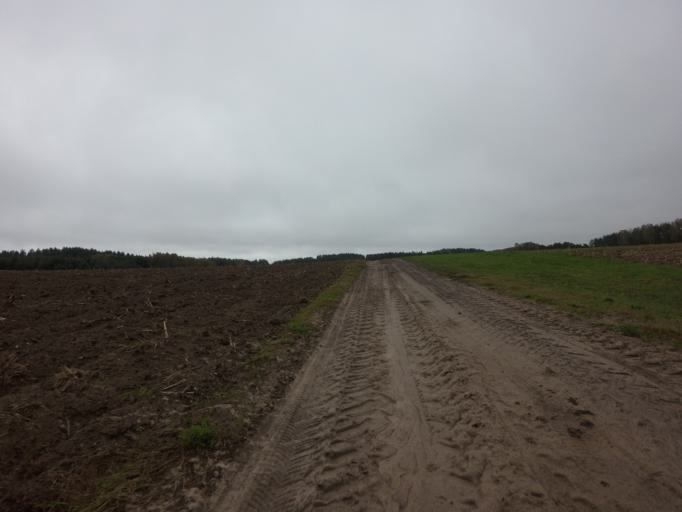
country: PL
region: Pomeranian Voivodeship
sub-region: Powiat kartuski
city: Stezyca
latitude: 54.1682
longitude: 17.9340
